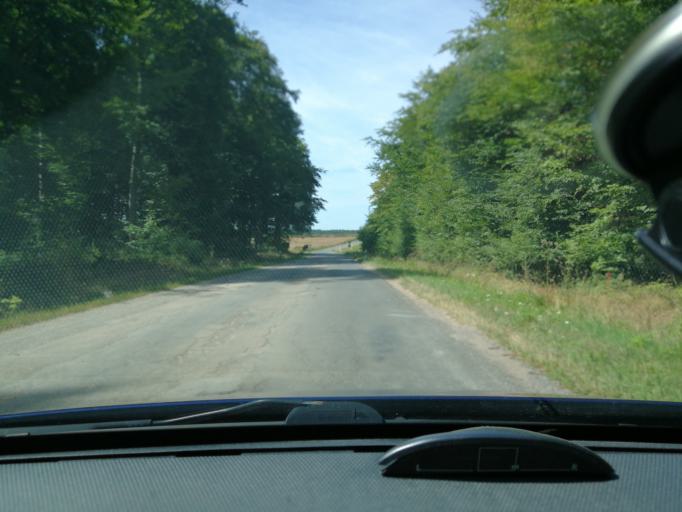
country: DE
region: Rheinland-Pfalz
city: Dodenburg
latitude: 49.9191
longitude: 6.7874
